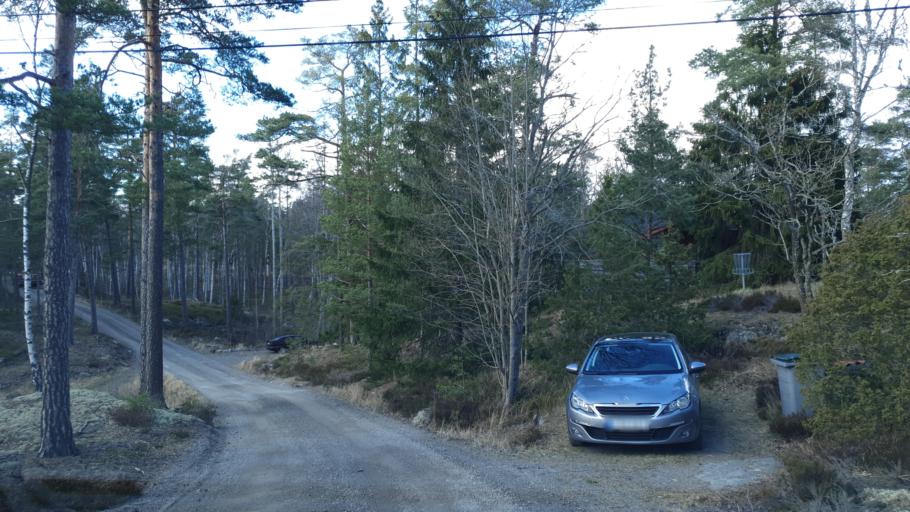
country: SE
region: Stockholm
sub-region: Varmdo Kommun
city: Holo
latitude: 59.2710
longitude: 18.6397
